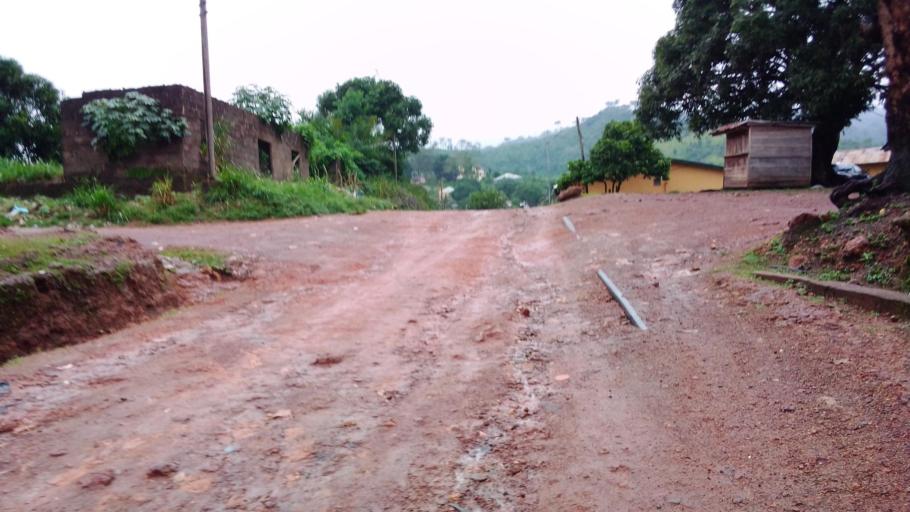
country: SL
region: Eastern Province
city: Kenema
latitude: 7.8917
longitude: -11.1869
